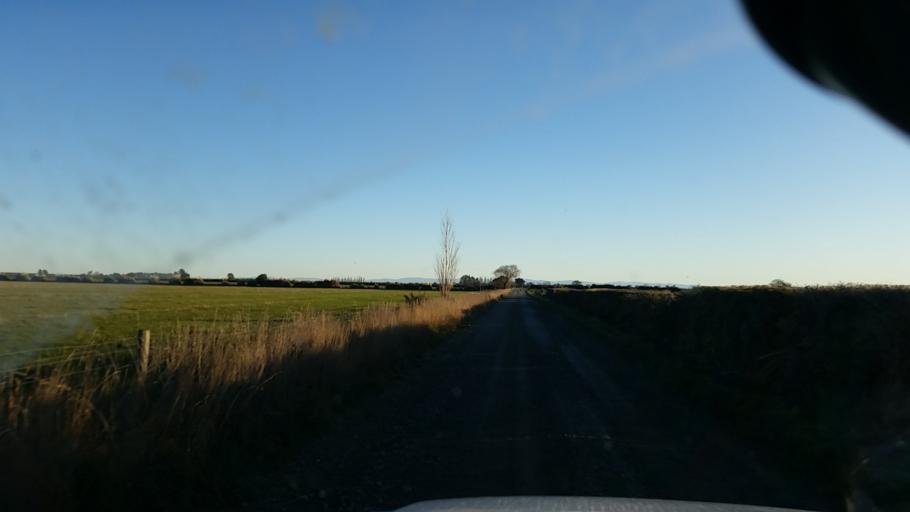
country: NZ
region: Canterbury
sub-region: Ashburton District
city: Tinwald
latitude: -44.0318
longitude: 171.6991
